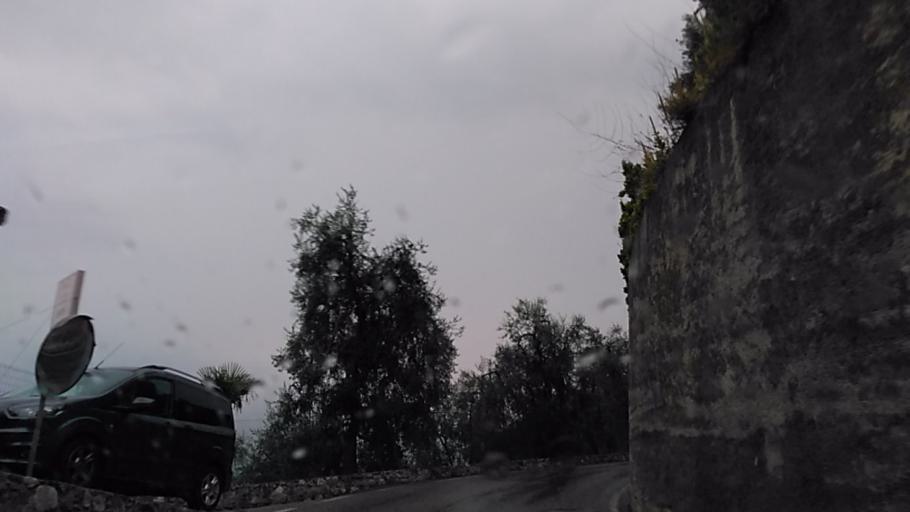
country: IT
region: Lombardy
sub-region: Provincia di Brescia
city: Limone sul Garda
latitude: 45.7991
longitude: 10.7813
